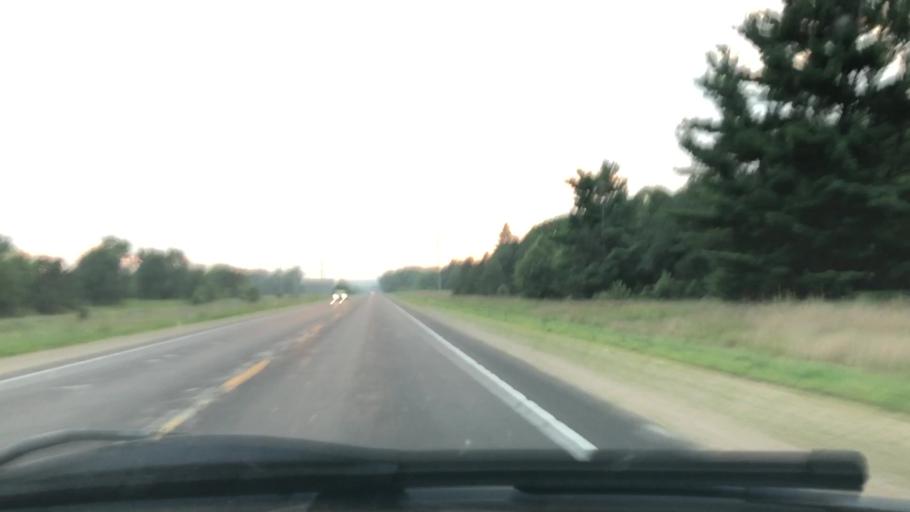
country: US
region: Wisconsin
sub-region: Sauk County
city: Spring Green
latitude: 43.1973
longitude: -90.2355
